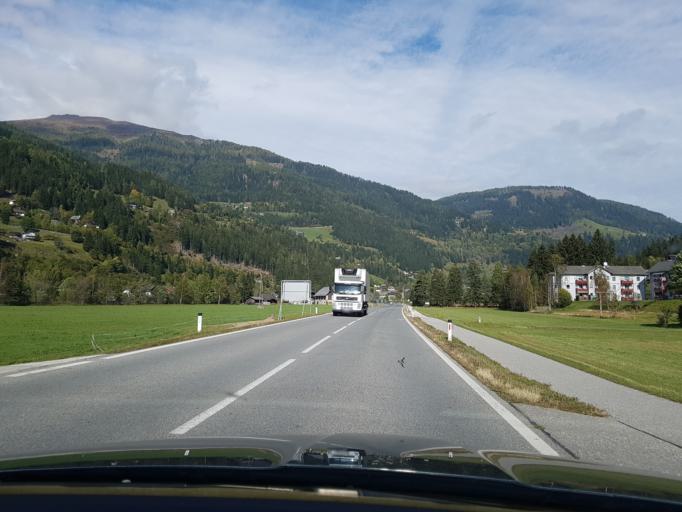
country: AT
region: Carinthia
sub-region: Politischer Bezirk Spittal an der Drau
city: Kleinkirchheim
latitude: 46.8199
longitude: 13.8625
